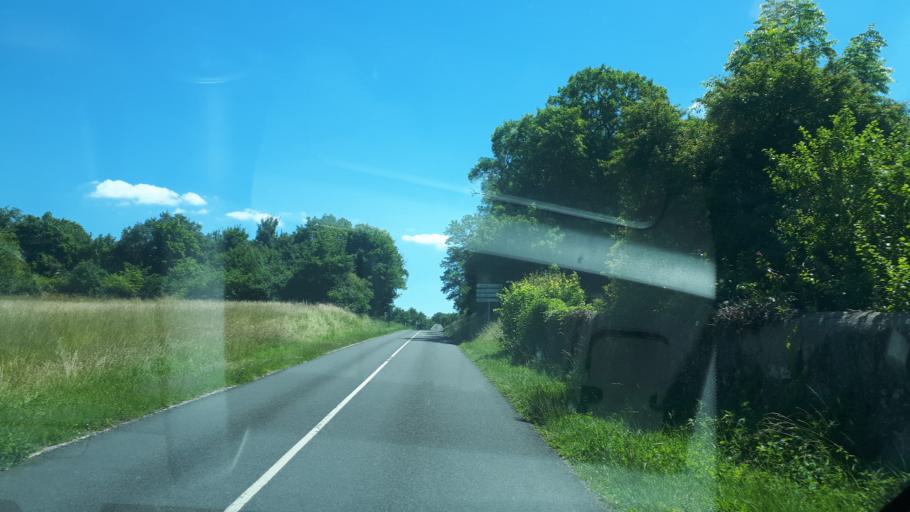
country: FR
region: Centre
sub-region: Departement du Loir-et-Cher
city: Chouzy-sur-Cisse
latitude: 47.5665
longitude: 1.2158
